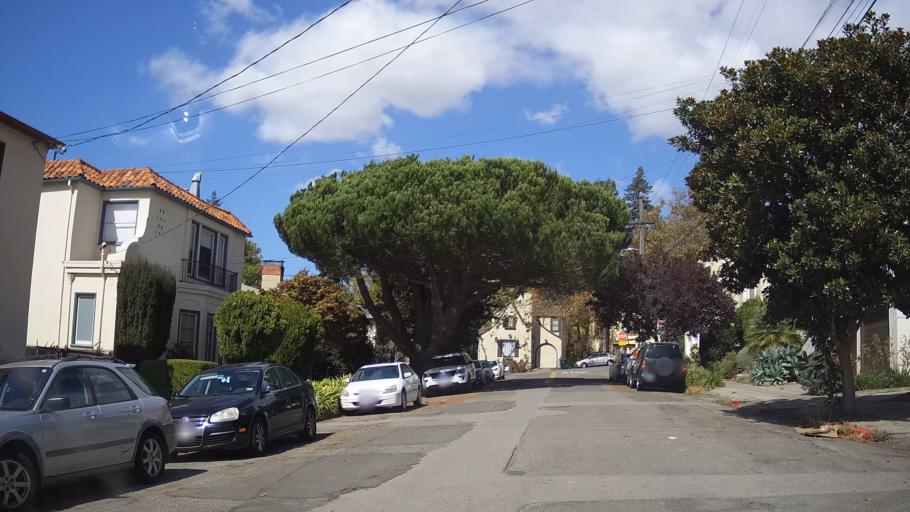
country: US
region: California
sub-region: Alameda County
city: Berkeley
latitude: 37.8785
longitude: -122.2629
